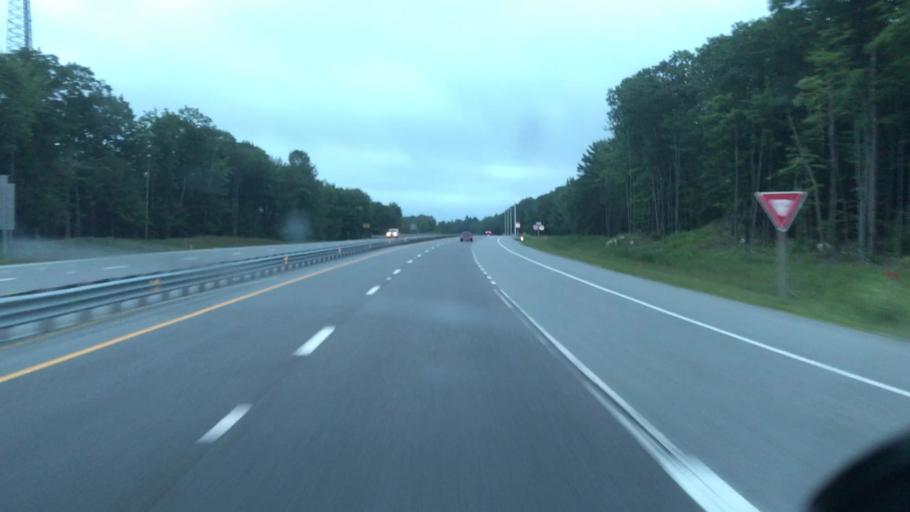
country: US
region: Maine
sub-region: Androscoggin County
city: Lewiston
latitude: 44.0712
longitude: -70.1800
